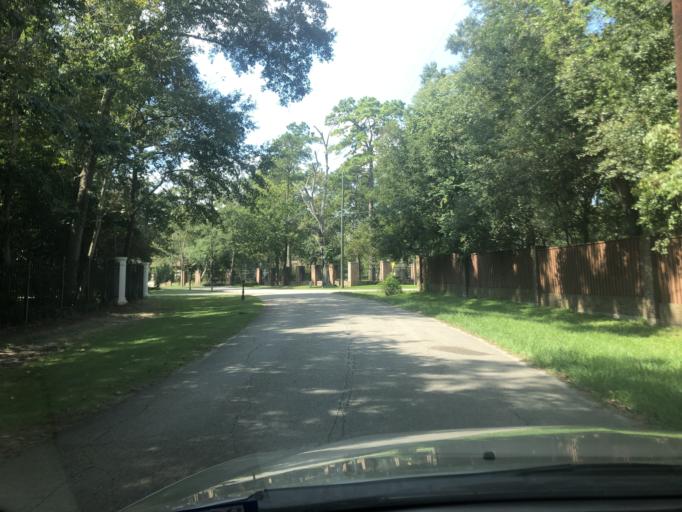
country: US
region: Texas
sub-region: Harris County
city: Bunker Hill Village
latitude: 29.7510
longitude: -95.5453
